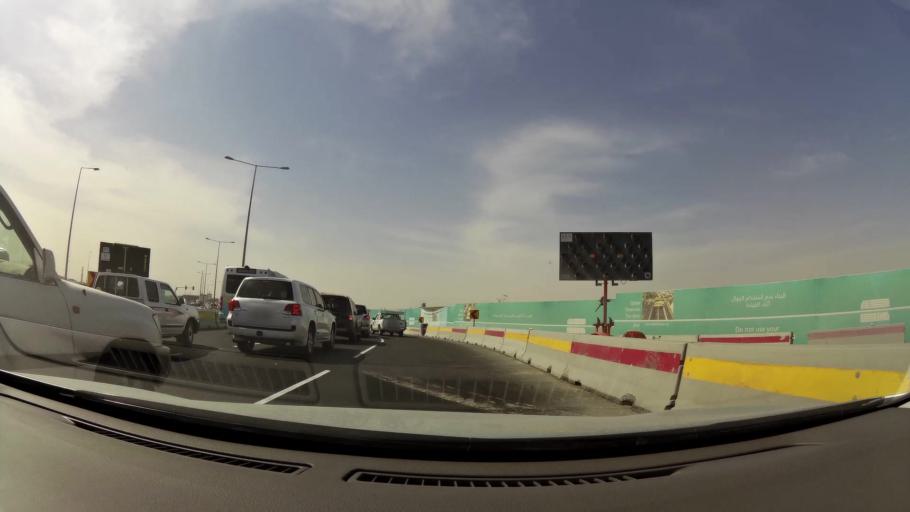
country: QA
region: Baladiyat ar Rayyan
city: Ar Rayyan
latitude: 25.3061
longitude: 51.4140
